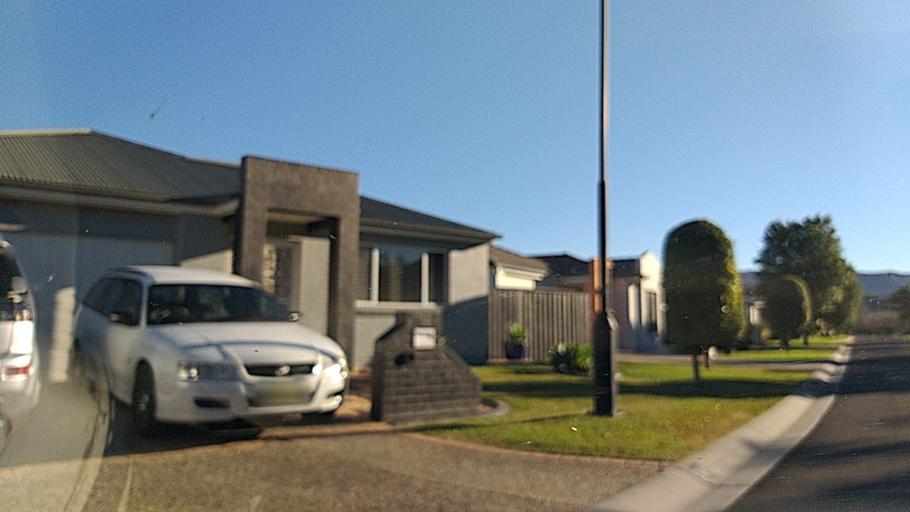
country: AU
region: New South Wales
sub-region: Wollongong
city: Bulli
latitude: -34.3475
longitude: 150.9028
